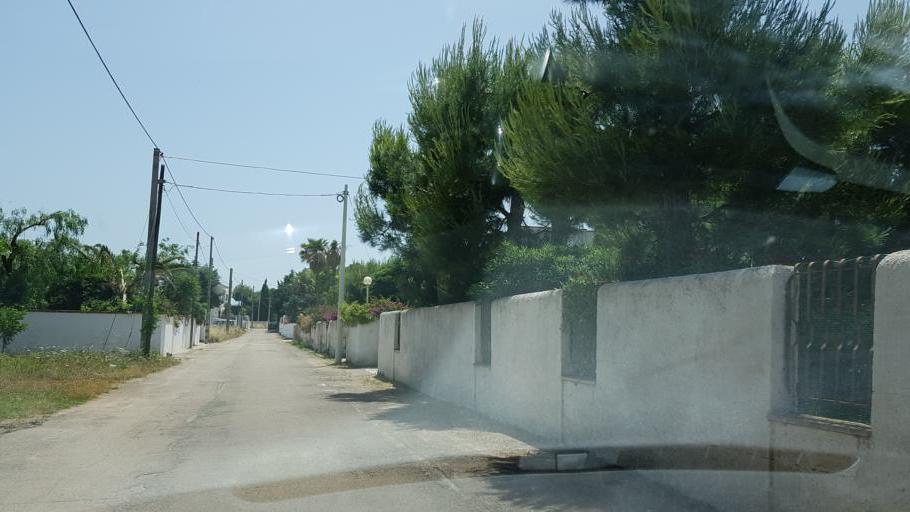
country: IT
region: Apulia
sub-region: Provincia di Lecce
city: Porto Cesareo
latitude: 40.2530
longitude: 17.9194
